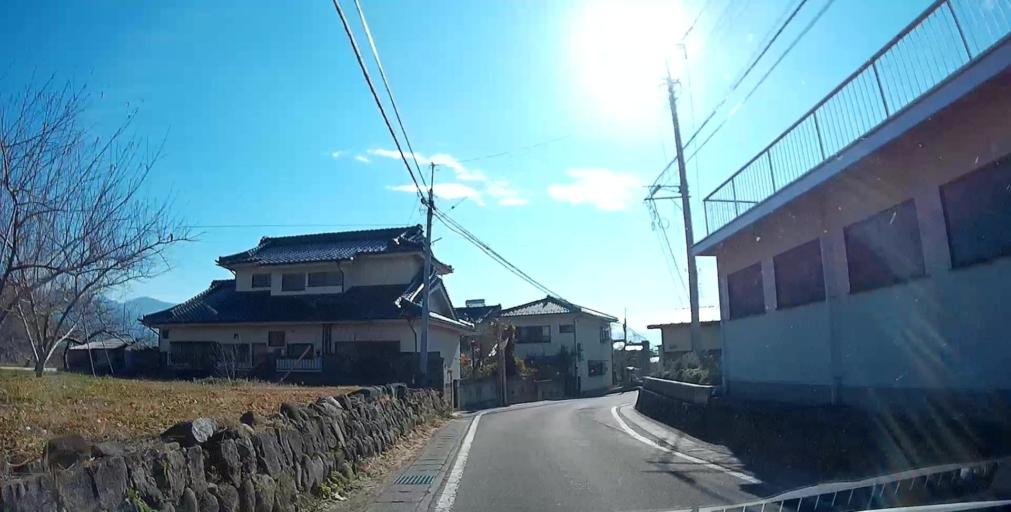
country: JP
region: Yamanashi
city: Enzan
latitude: 35.7349
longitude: 138.7186
